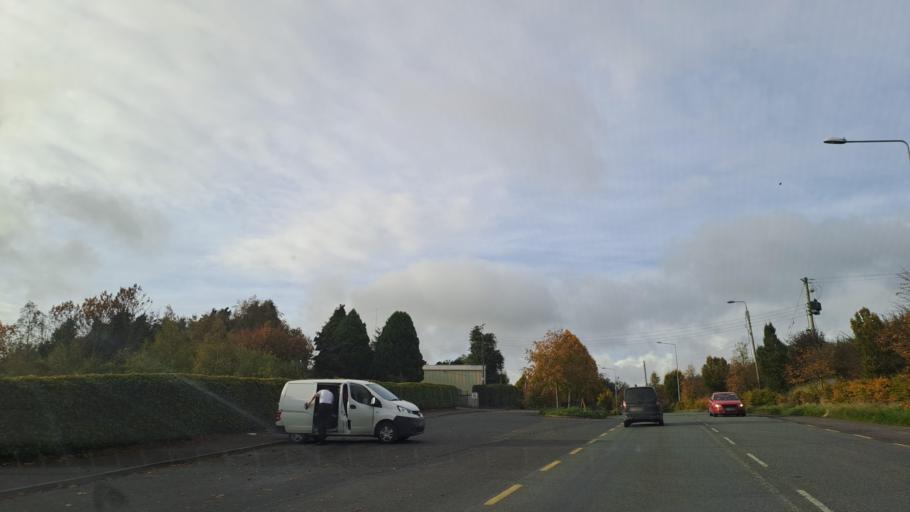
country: IE
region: Ulster
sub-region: An Cabhan
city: Kingscourt
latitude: 53.8174
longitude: -6.7408
